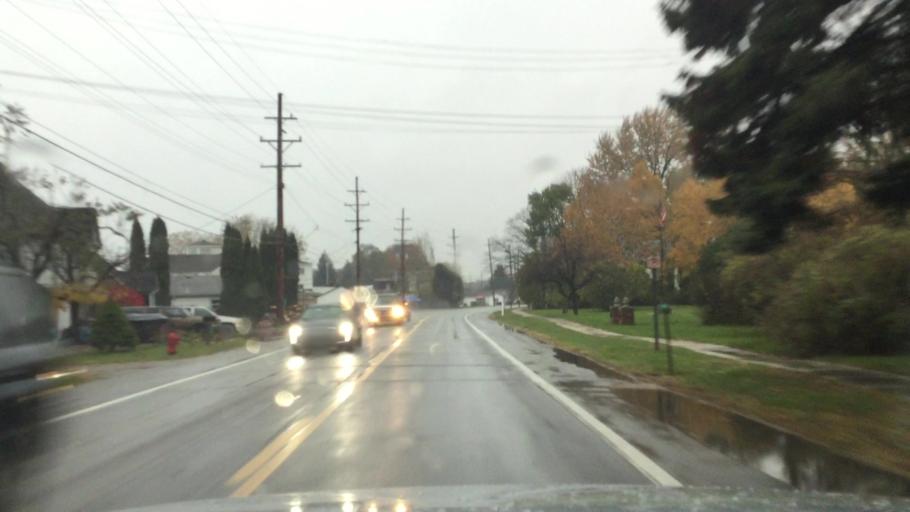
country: US
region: Michigan
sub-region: Saint Clair County
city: Algonac
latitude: 42.6194
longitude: -82.5634
